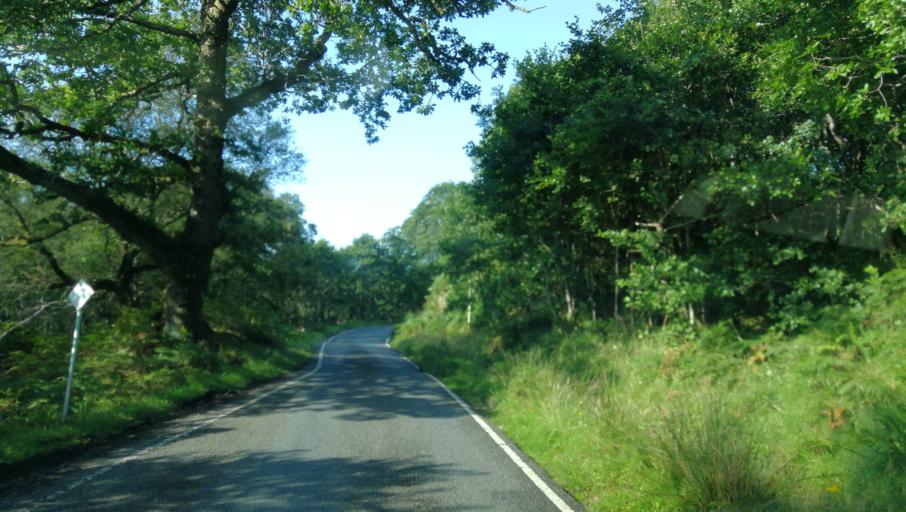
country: GB
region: Scotland
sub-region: Argyll and Bute
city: Isle Of Mull
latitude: 56.6801
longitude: -5.8321
